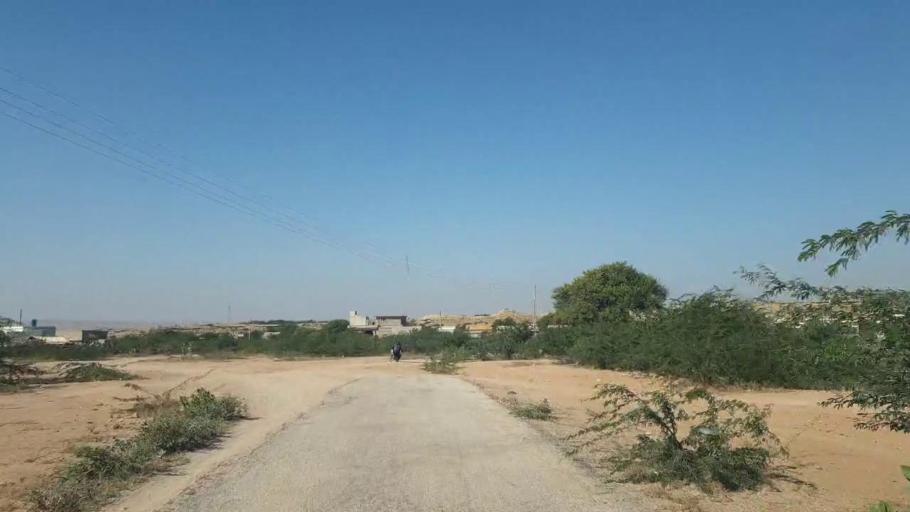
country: PK
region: Sindh
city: Gharo
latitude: 25.0899
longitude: 67.5363
